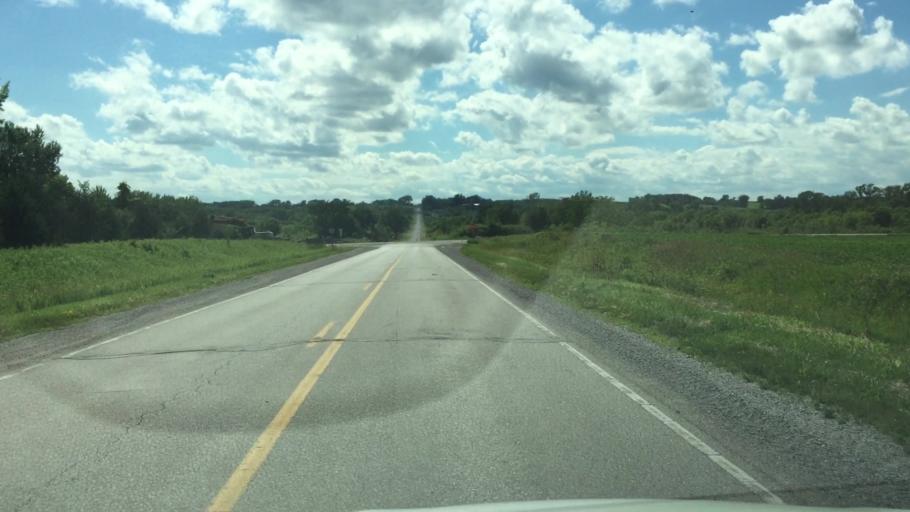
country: US
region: Iowa
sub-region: Linn County
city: Ely
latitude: 41.8323
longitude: -91.5482
